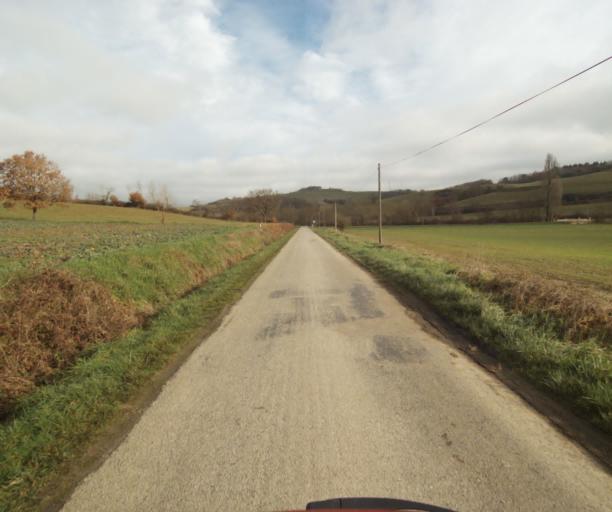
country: FR
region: Midi-Pyrenees
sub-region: Departement de l'Ariege
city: Saverdun
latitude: 43.1894
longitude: 1.5208
